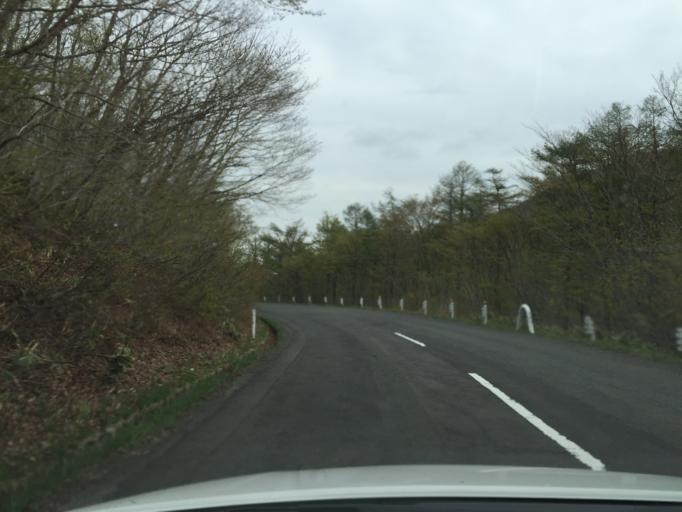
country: JP
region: Fukushima
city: Inawashiro
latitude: 37.5858
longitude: 140.2440
